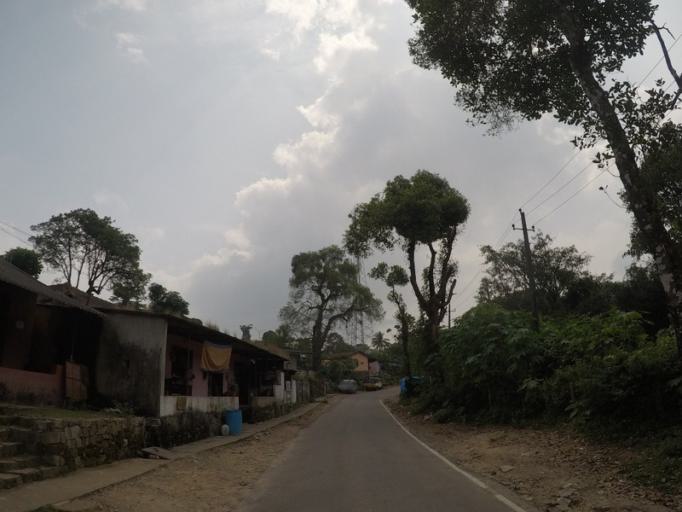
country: IN
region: Karnataka
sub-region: Chikmagalur
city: Mudigere
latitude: 13.1981
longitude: 75.4109
